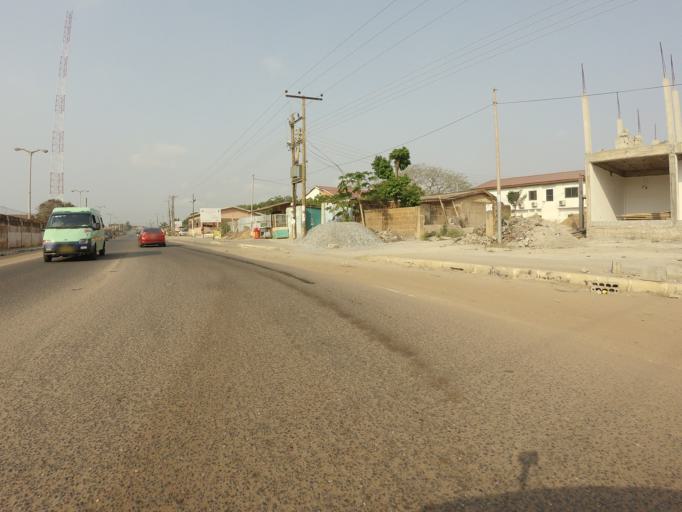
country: GH
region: Greater Accra
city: Teshi Old Town
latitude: 5.5749
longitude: -0.1461
